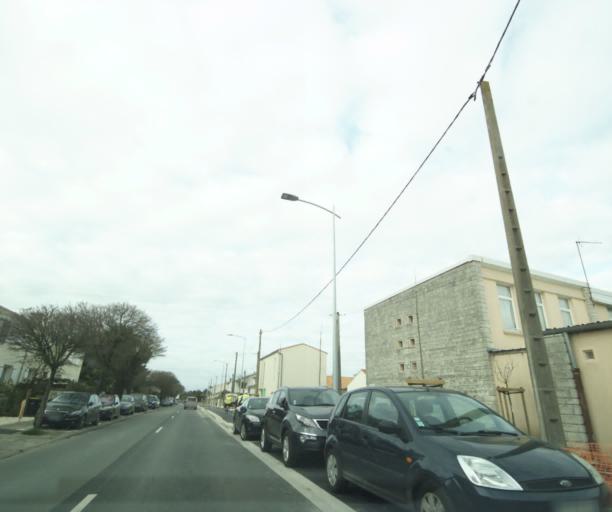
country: FR
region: Poitou-Charentes
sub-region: Departement de la Charente-Maritime
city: La Rochelle
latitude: 46.1701
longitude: -1.1639
